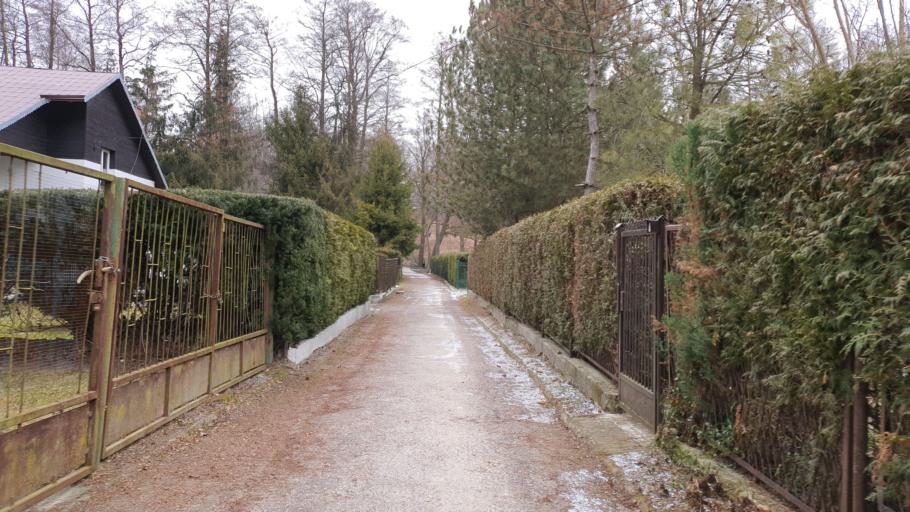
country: PL
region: Lublin Voivodeship
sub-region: Powiat pulawski
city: Naleczow
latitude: 51.2817
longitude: 22.2116
